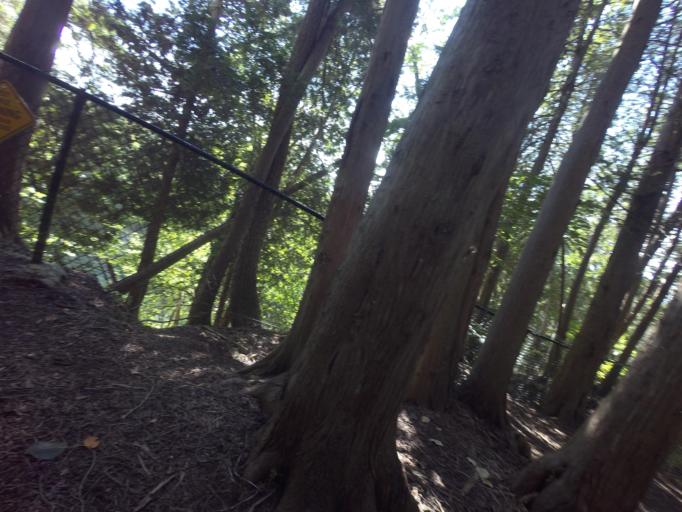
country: CA
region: Ontario
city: Waterloo
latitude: 43.6751
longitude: -80.4487
